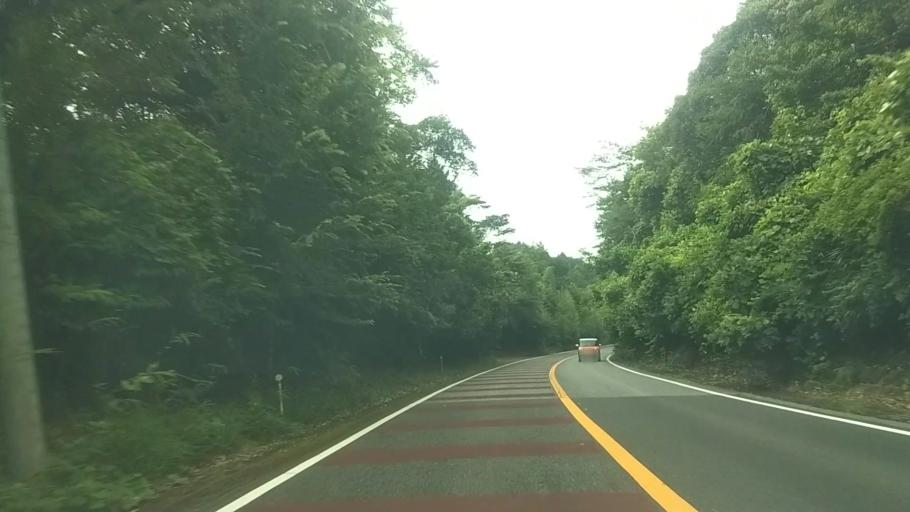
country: JP
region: Chiba
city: Kimitsu
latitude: 35.2351
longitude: 140.0080
